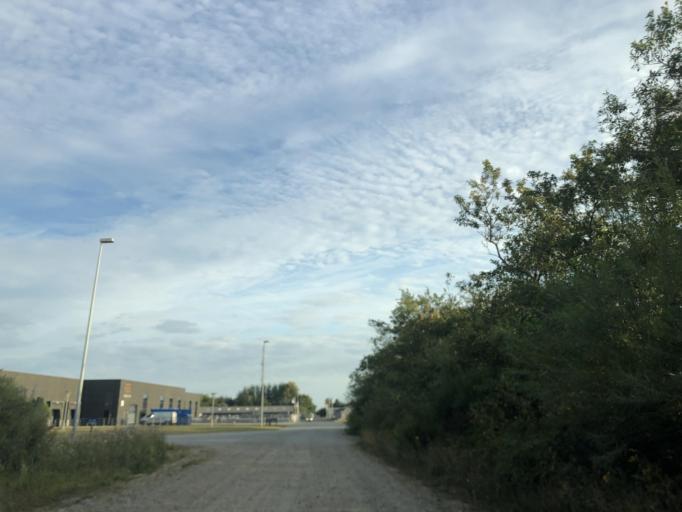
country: DK
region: Central Jutland
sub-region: Holstebro Kommune
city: Ulfborg
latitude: 56.2601
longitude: 8.3216
